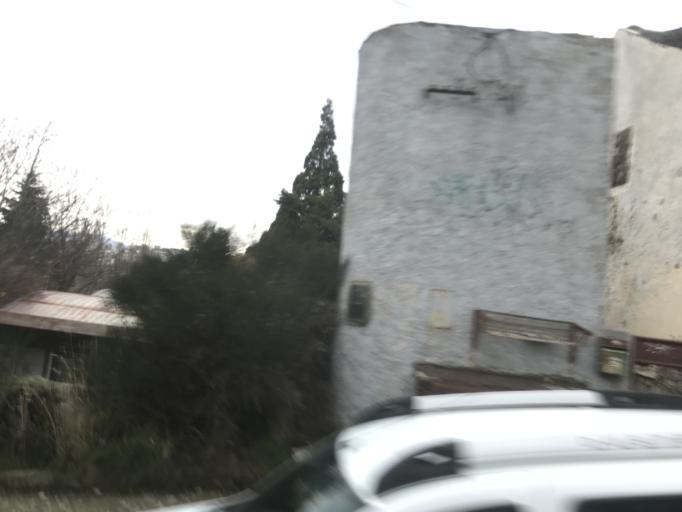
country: AR
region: Rio Negro
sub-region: Departamento de Bariloche
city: San Carlos de Bariloche
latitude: -41.1389
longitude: -71.3150
